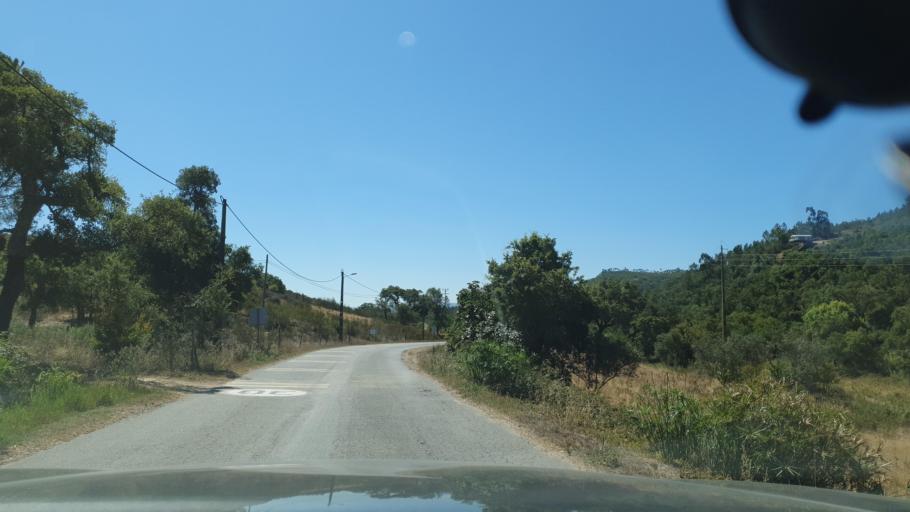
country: PT
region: Beja
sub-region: Odemira
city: Sao Teotonio
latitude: 37.4991
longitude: -8.6533
